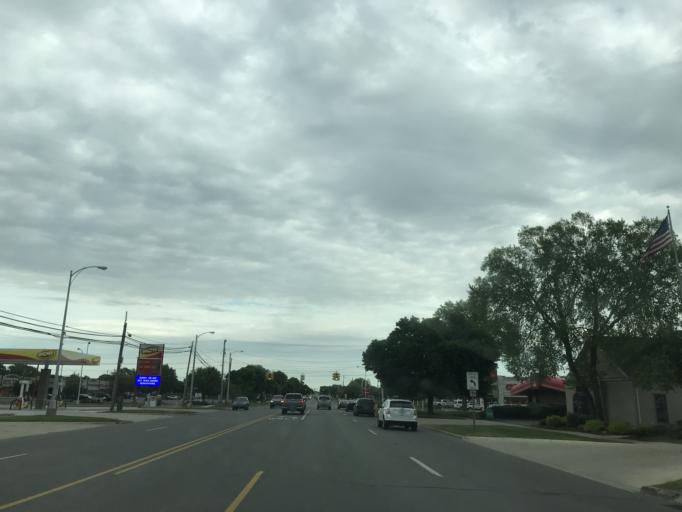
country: US
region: Michigan
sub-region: Wayne County
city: Woodhaven
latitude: 42.1410
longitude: -83.2129
